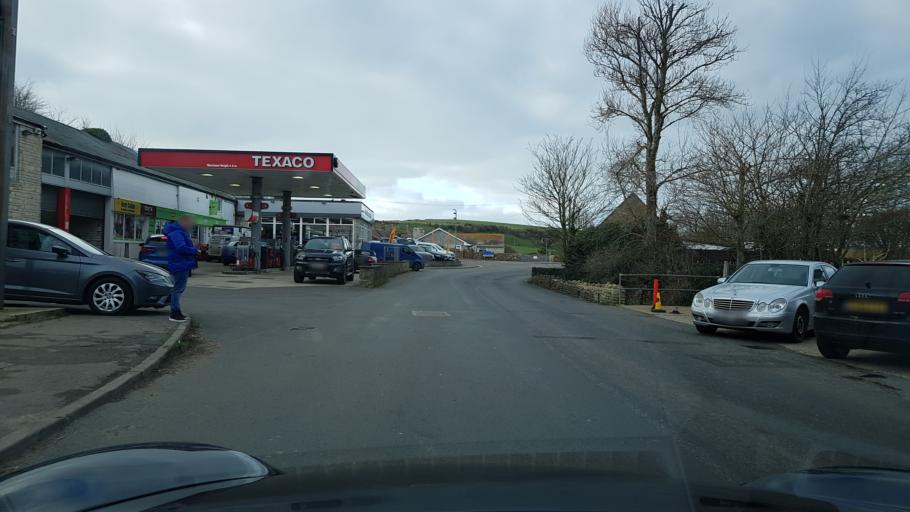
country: GB
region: England
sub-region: Dorset
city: Bridport
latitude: 50.7009
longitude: -2.7264
